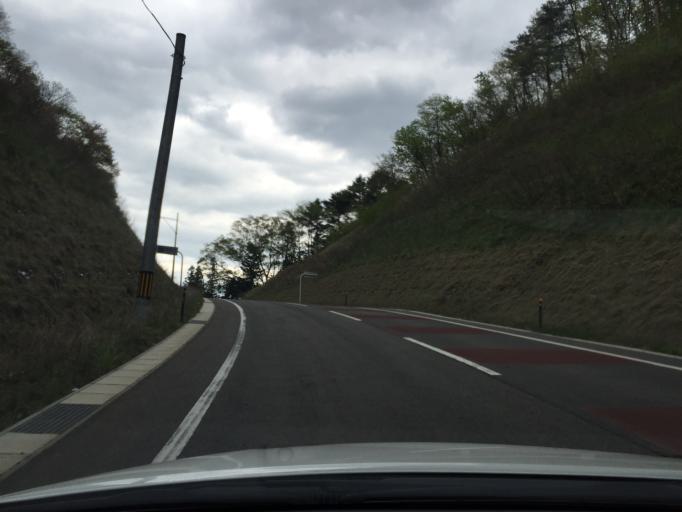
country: JP
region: Fukushima
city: Yanagawamachi-saiwaicho
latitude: 37.7476
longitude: 140.7005
